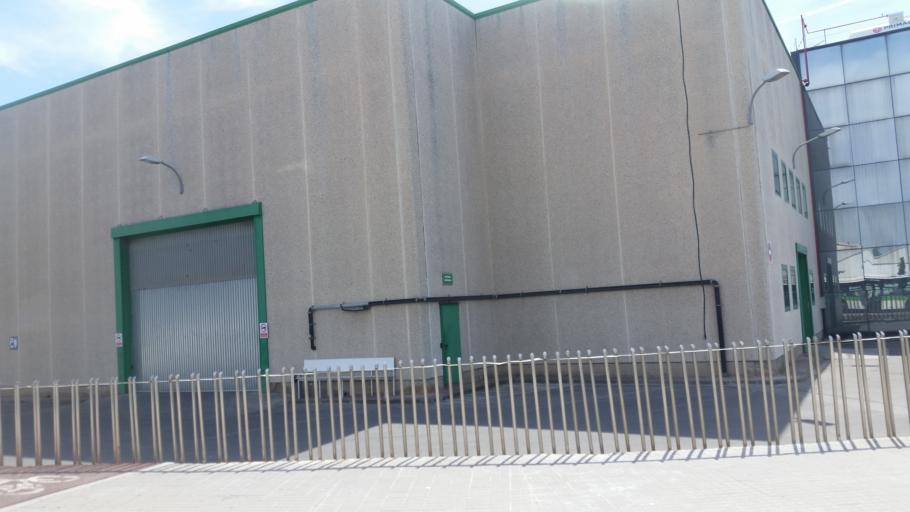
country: ES
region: Catalonia
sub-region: Provincia de Barcelona
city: El Prat de Llobregat
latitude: 41.3303
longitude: 2.0858
